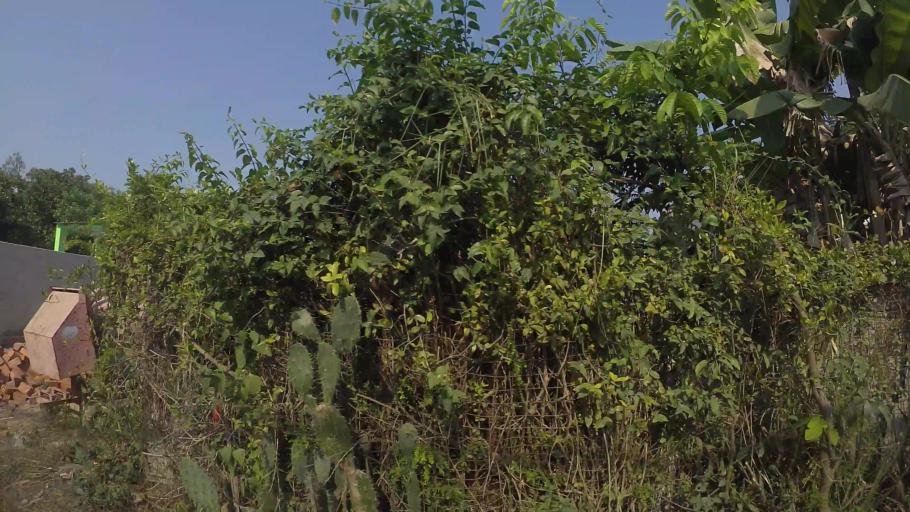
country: VN
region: Da Nang
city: Ngu Hanh Son
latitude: 15.9571
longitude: 108.2647
